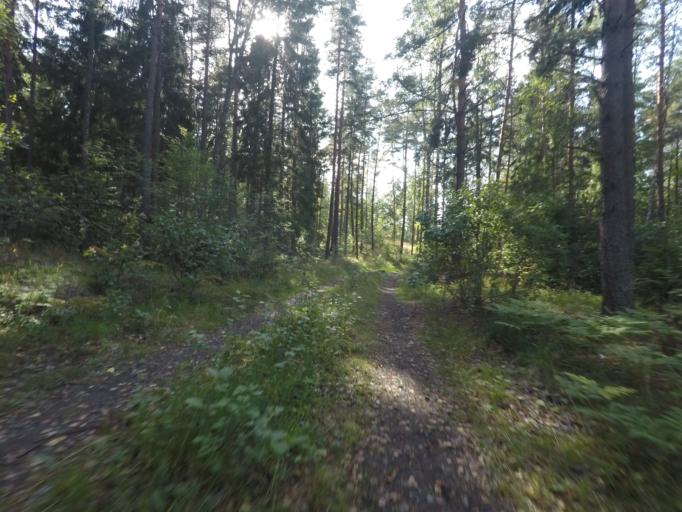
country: SE
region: Soedermanland
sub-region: Eskilstuna Kommun
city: Kvicksund
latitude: 59.4329
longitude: 16.2588
